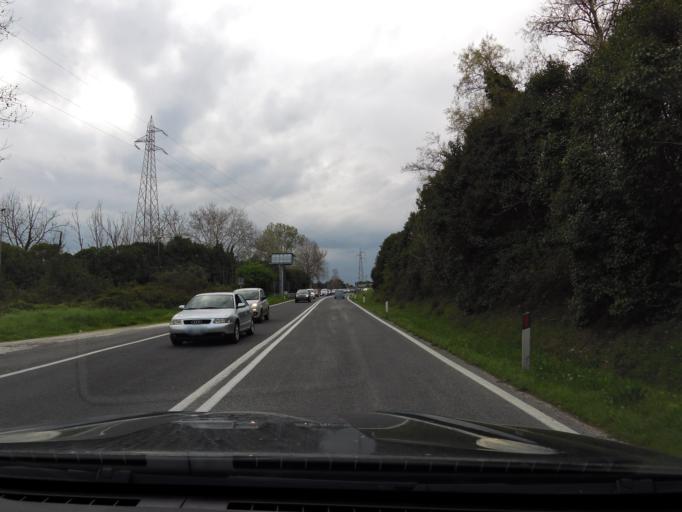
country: IT
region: The Marches
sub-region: Provincia di Ancona
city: Loreto Stazione
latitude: 43.4388
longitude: 13.6398
